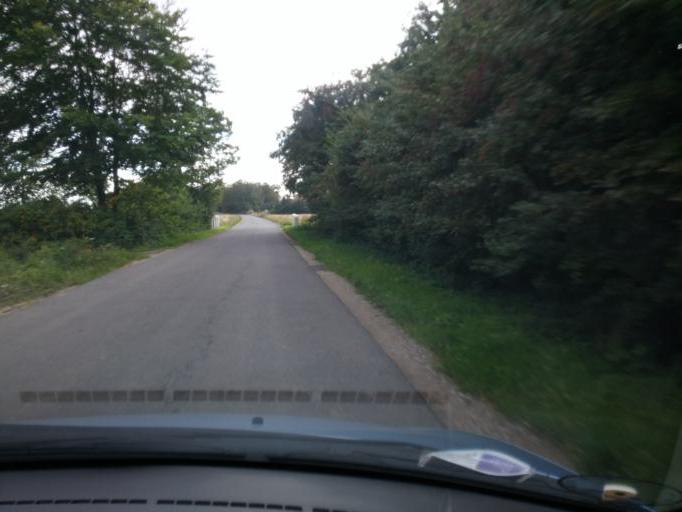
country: DK
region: South Denmark
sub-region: Kerteminde Kommune
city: Munkebo
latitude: 55.4188
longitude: 10.5604
